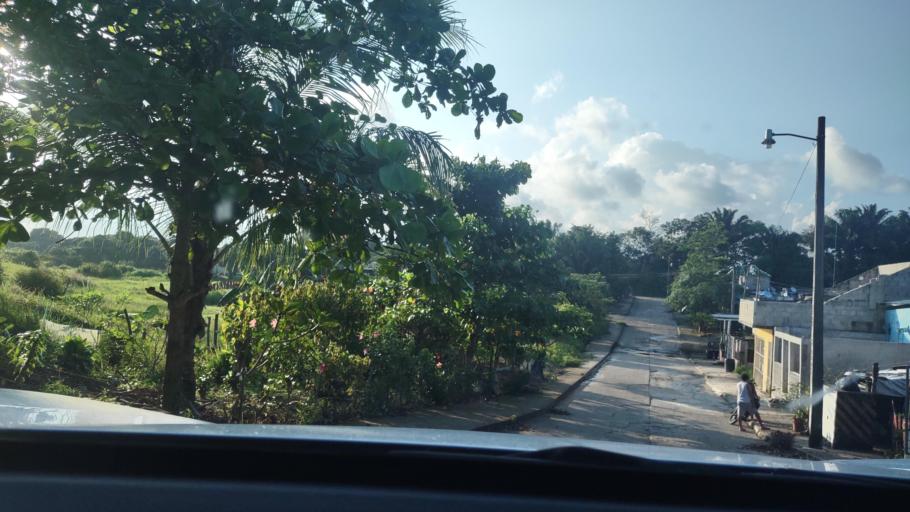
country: MX
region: Veracruz
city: Las Choapas
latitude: 17.9346
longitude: -94.1149
